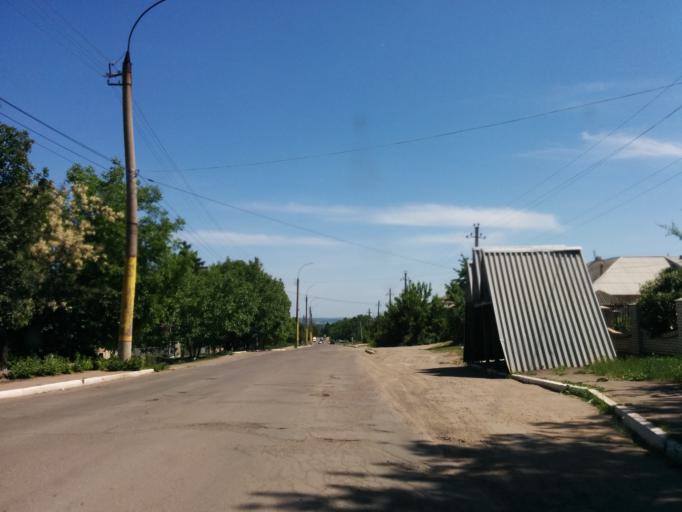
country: MD
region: Raionul Soroca
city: Soroca
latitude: 48.1624
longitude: 28.2741
